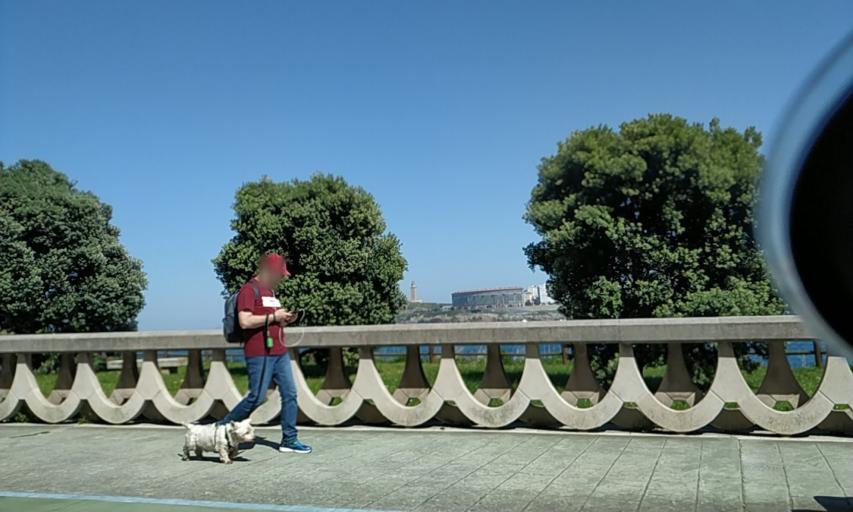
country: ES
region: Galicia
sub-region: Provincia da Coruna
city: A Coruna
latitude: 43.3732
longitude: -8.4194
